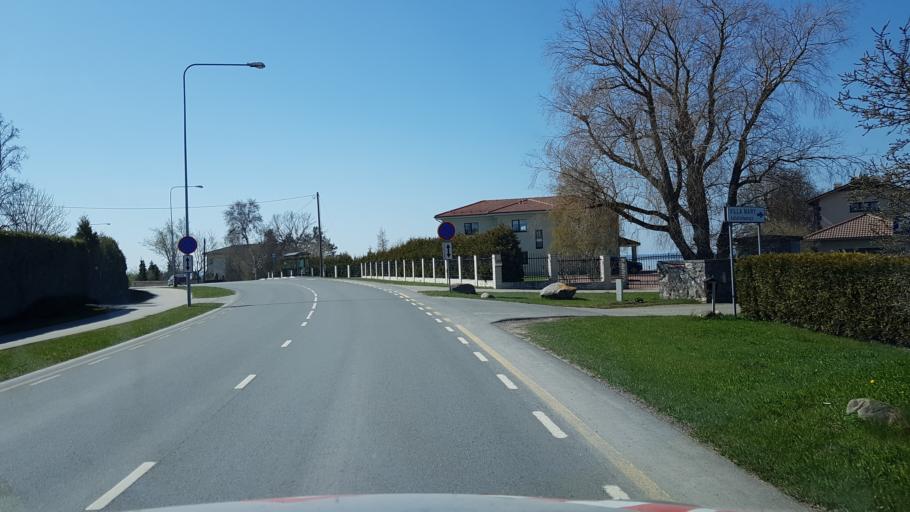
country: EE
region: Harju
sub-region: Viimsi vald
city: Rummu
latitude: 59.5565
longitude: 24.7950
